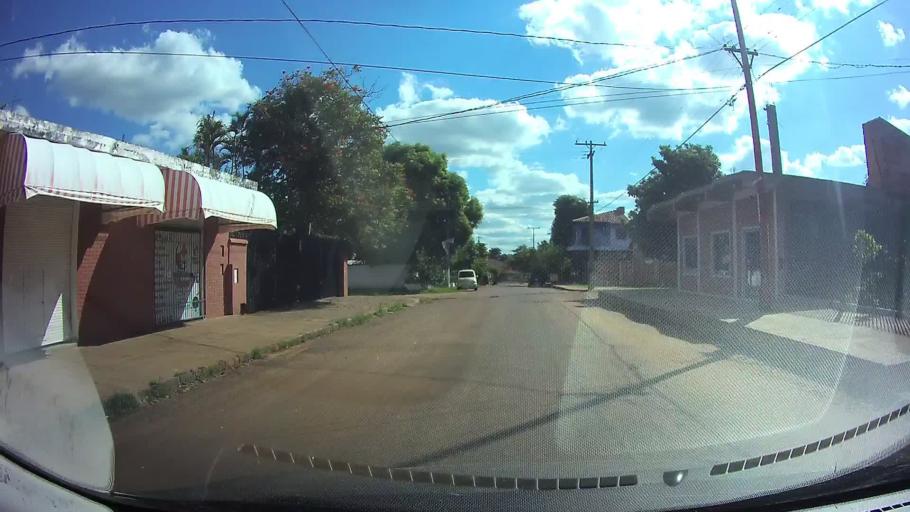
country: PY
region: Central
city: Itaugua
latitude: -25.3897
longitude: -57.3499
